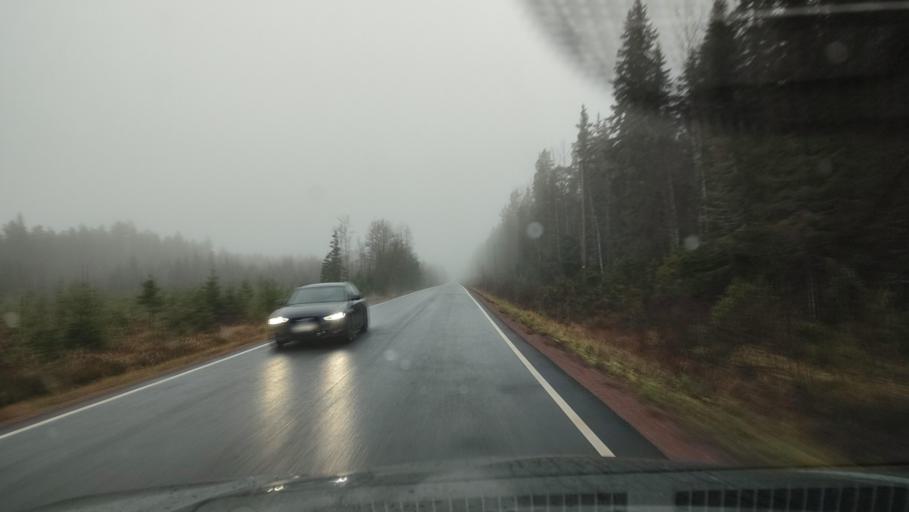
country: FI
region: Southern Ostrobothnia
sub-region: Suupohja
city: Karijoki
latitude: 62.1717
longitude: 21.7540
